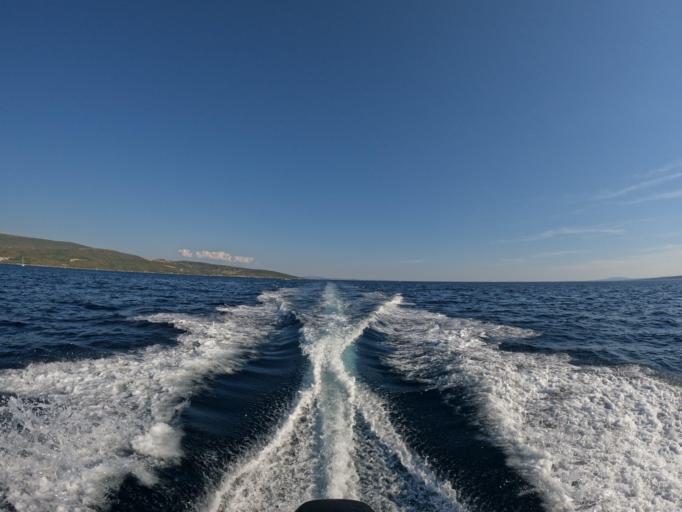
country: HR
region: Primorsko-Goranska
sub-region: Grad Krk
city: Krk
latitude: 45.0118
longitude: 14.5891
